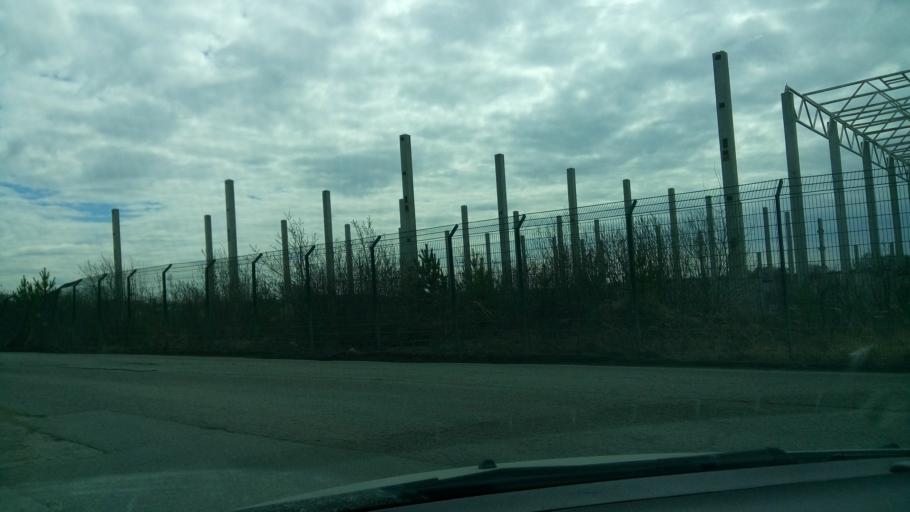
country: RU
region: Sverdlovsk
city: Verkhnyaya Pyshma
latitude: 56.9647
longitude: 60.6665
